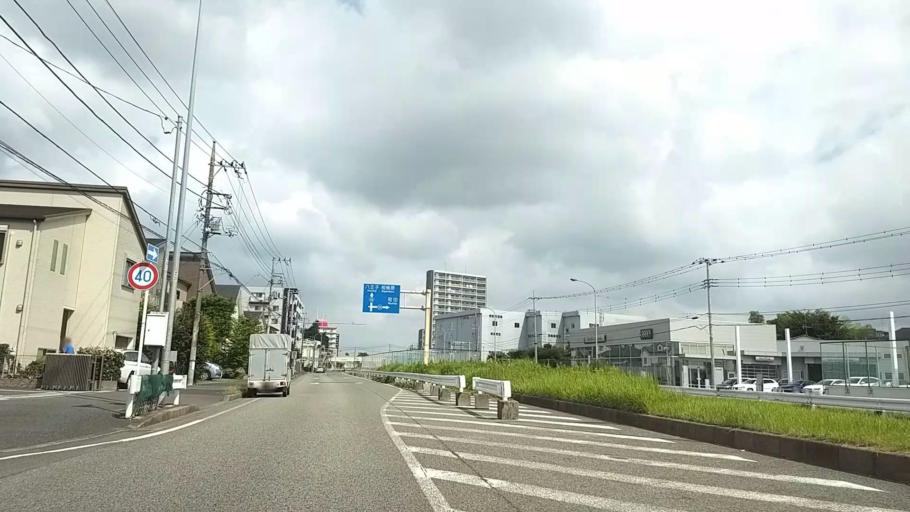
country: JP
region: Tokyo
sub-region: Machida-shi
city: Machida
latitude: 35.5148
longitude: 139.4569
